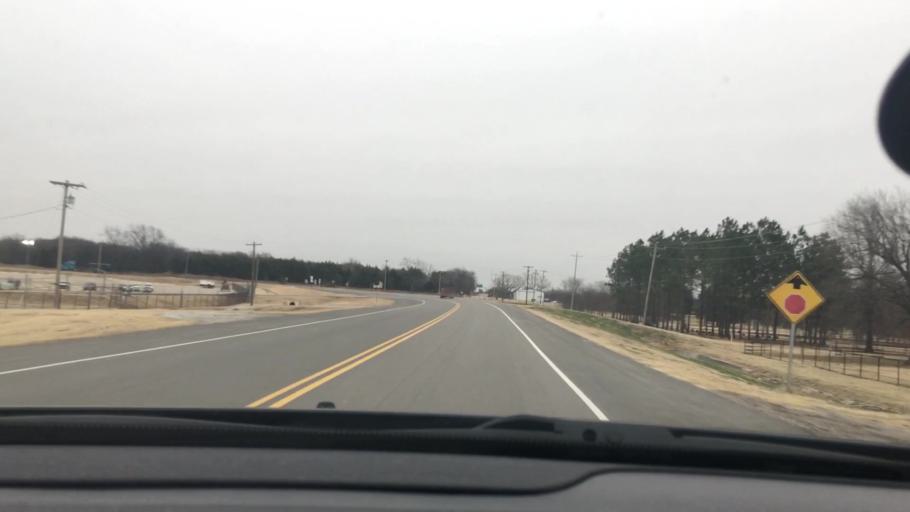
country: US
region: Oklahoma
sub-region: Garvin County
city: Wynnewood
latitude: 34.6226
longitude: -97.1659
